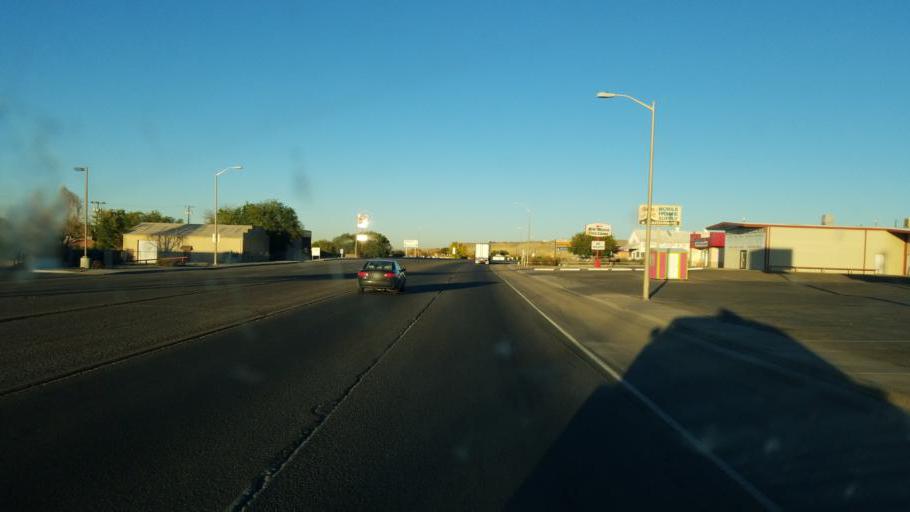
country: US
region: New Mexico
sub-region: San Juan County
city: Farmington
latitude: 36.7322
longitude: -108.2387
